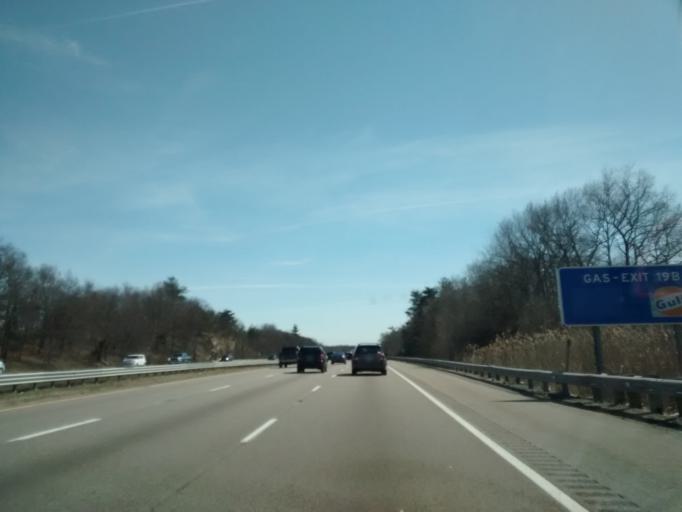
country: US
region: Massachusetts
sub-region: Norfolk County
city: Avon
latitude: 42.1344
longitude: -71.0644
